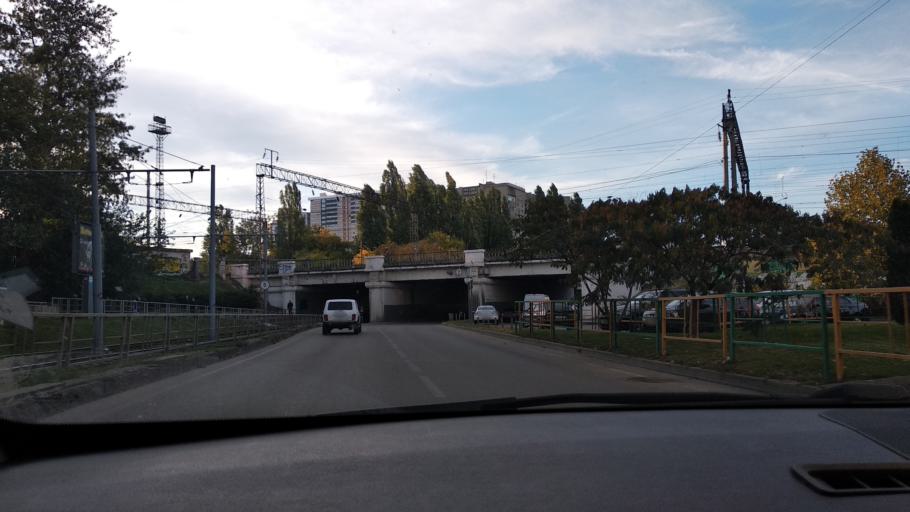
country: RU
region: Krasnodarskiy
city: Krasnodar
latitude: 45.0215
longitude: 38.9983
